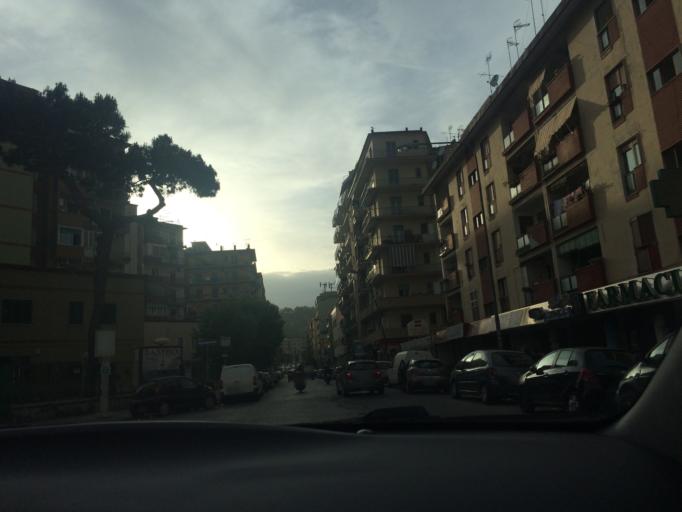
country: IT
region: Campania
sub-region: Provincia di Napoli
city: Bagnoli
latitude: 40.8298
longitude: 14.1964
